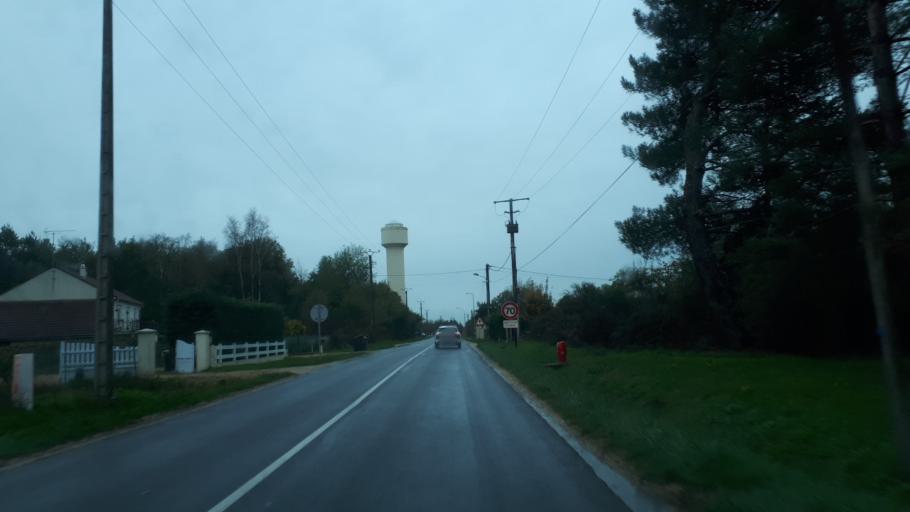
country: FR
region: Centre
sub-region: Departement du Loir-et-Cher
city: Gievres
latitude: 47.2876
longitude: 1.6695
